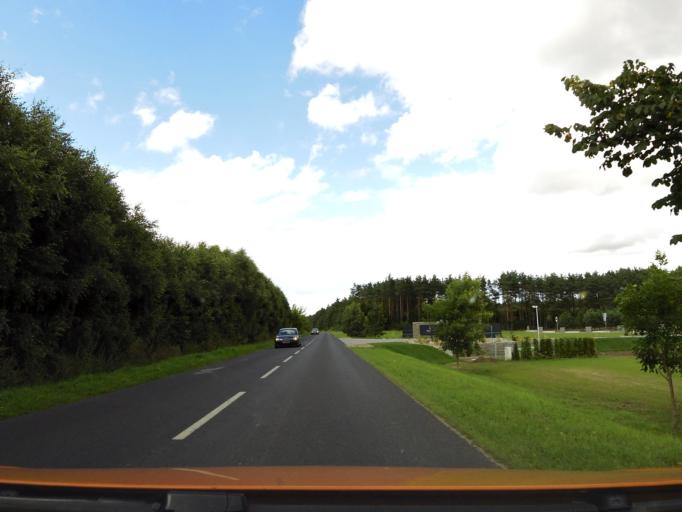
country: PL
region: West Pomeranian Voivodeship
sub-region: Powiat kolobrzeski
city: Kolobrzeg
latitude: 54.0998
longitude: 15.5797
